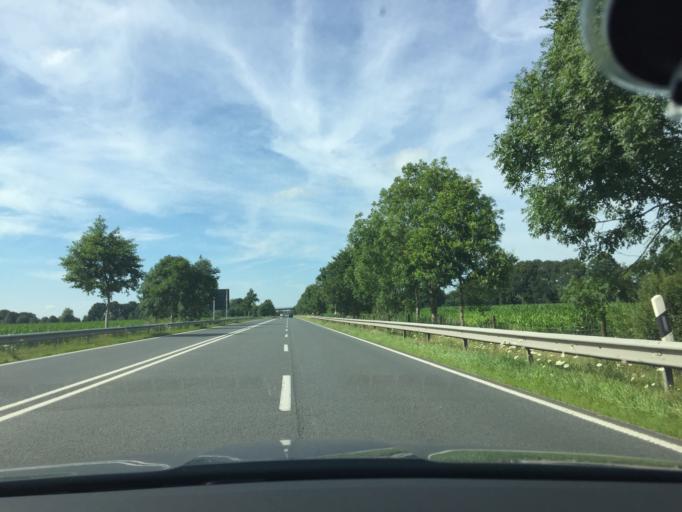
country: DE
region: Lower Saxony
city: Schortens
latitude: 53.5658
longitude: 7.9380
